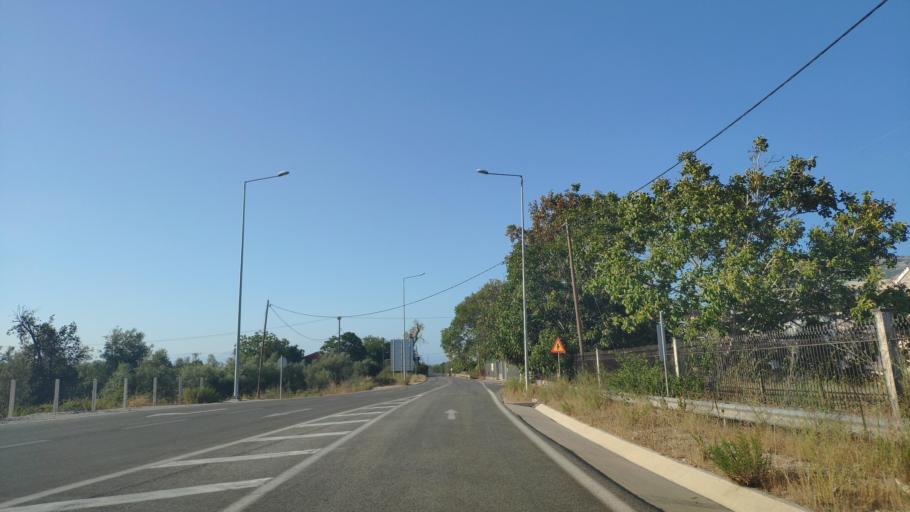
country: GR
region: West Greece
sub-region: Nomos Aitolias kai Akarnanias
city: Vonitsa
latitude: 38.8935
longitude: 20.8999
